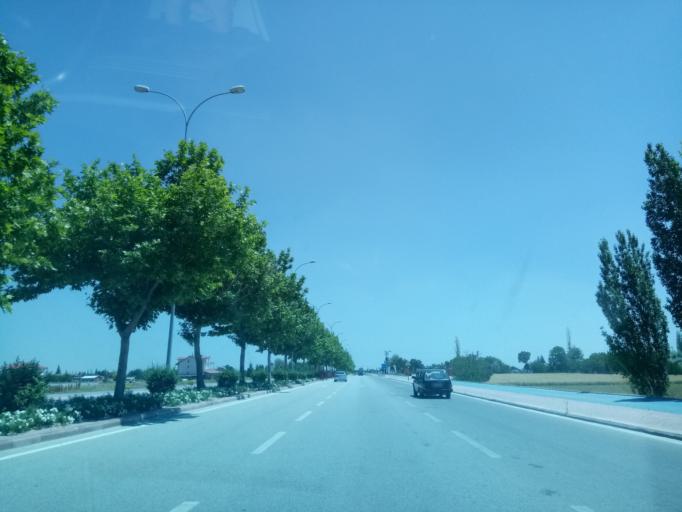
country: TR
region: Konya
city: Meram
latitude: 37.8120
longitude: 32.4393
